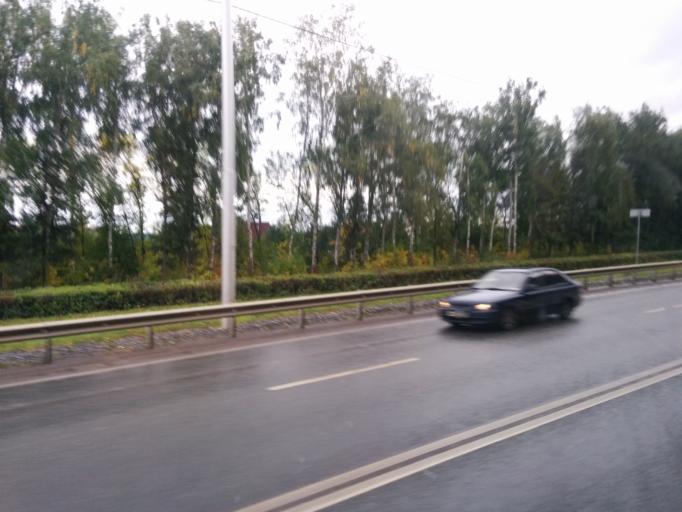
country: RU
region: Bashkortostan
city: Ufa
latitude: 54.5688
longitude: 55.8954
